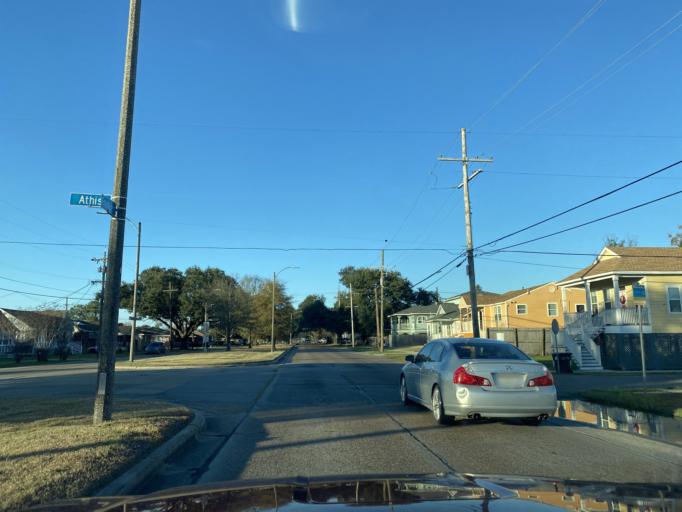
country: US
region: Louisiana
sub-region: Orleans Parish
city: New Orleans
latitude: 30.0182
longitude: -90.0514
